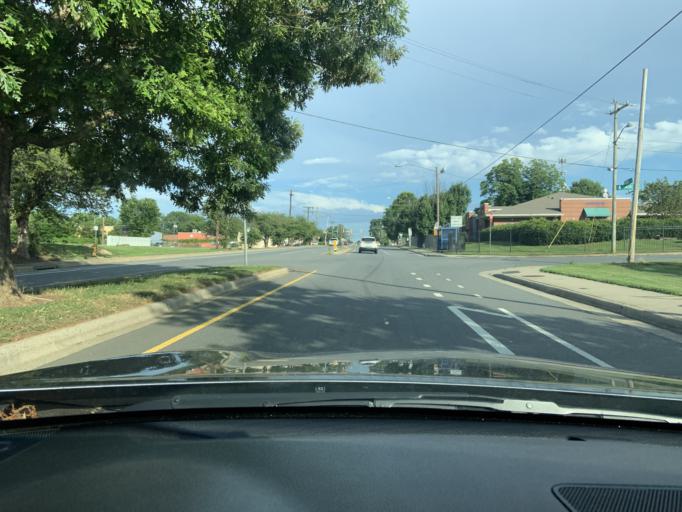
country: US
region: North Carolina
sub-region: Mecklenburg County
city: Charlotte
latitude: 35.2068
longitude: -80.8710
